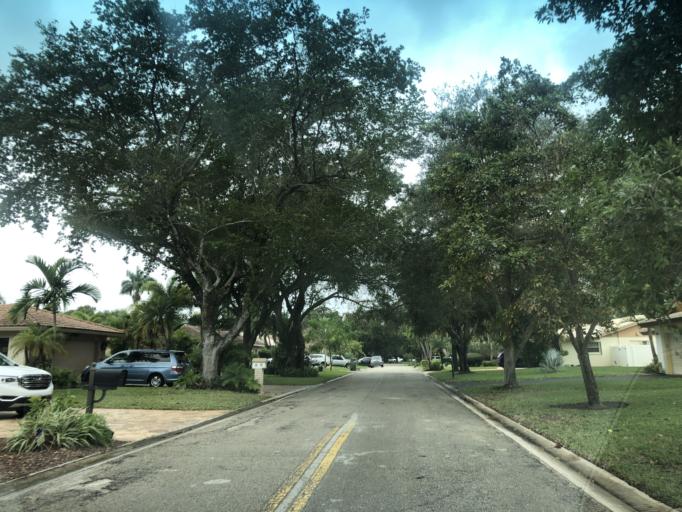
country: US
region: Florida
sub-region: Broward County
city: North Lauderdale
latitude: 26.2318
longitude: -80.2347
